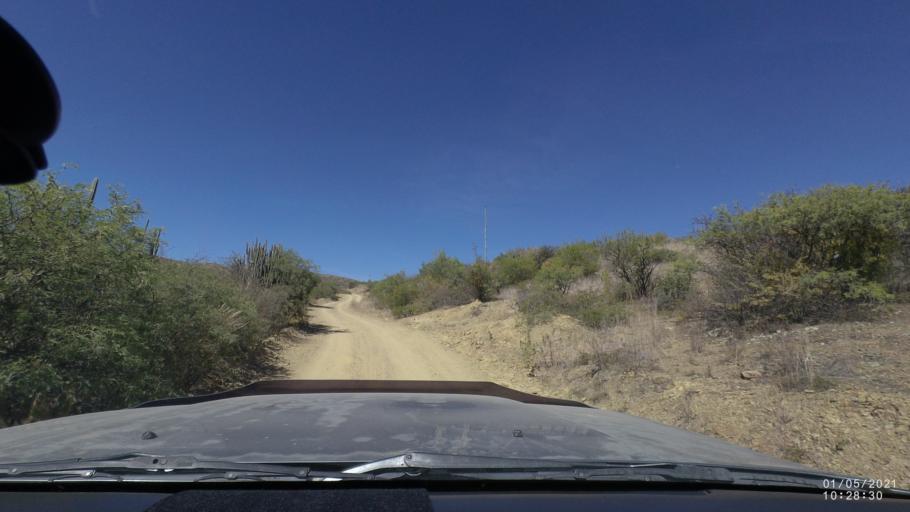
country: BO
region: Cochabamba
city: Capinota
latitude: -17.5895
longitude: -66.1895
